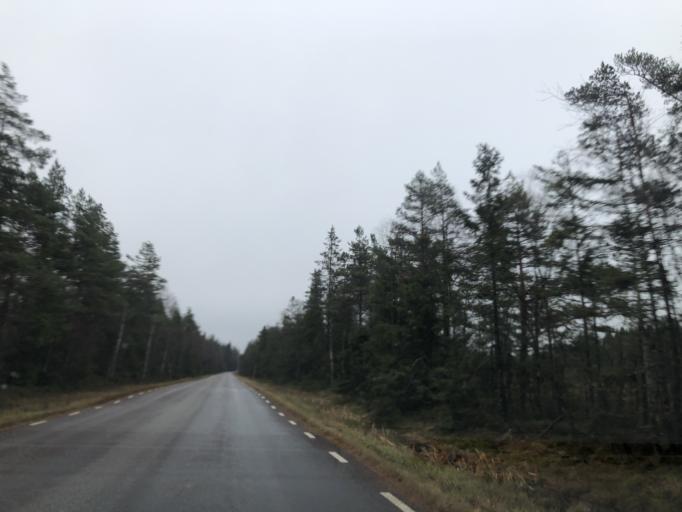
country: SE
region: Vaestra Goetaland
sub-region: Ulricehamns Kommun
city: Ulricehamn
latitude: 57.7568
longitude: 13.5022
